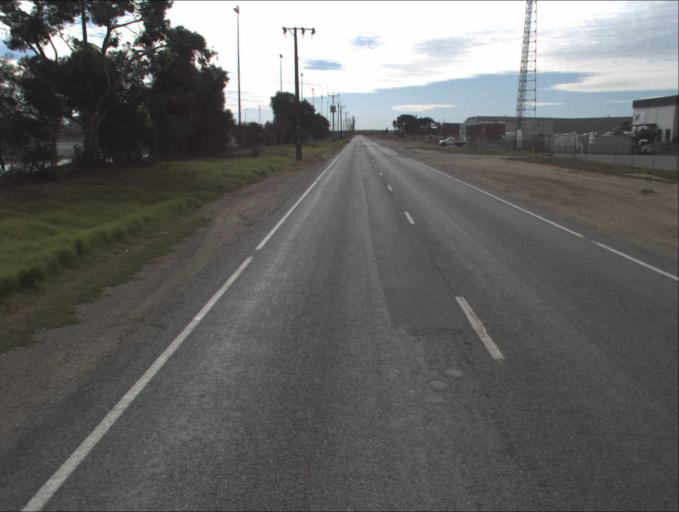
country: AU
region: South Australia
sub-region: Port Adelaide Enfield
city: Birkenhead
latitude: -34.8281
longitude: 138.5190
